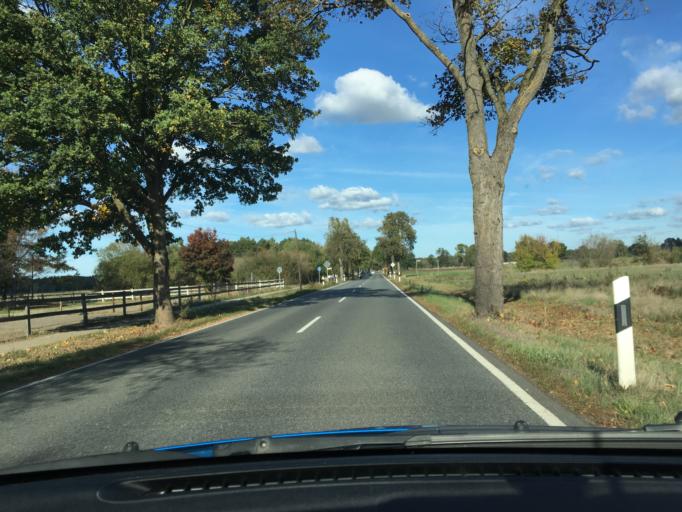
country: DE
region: Lower Saxony
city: Isernhagen Farster Bauerschaft
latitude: 52.5121
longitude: 9.8592
